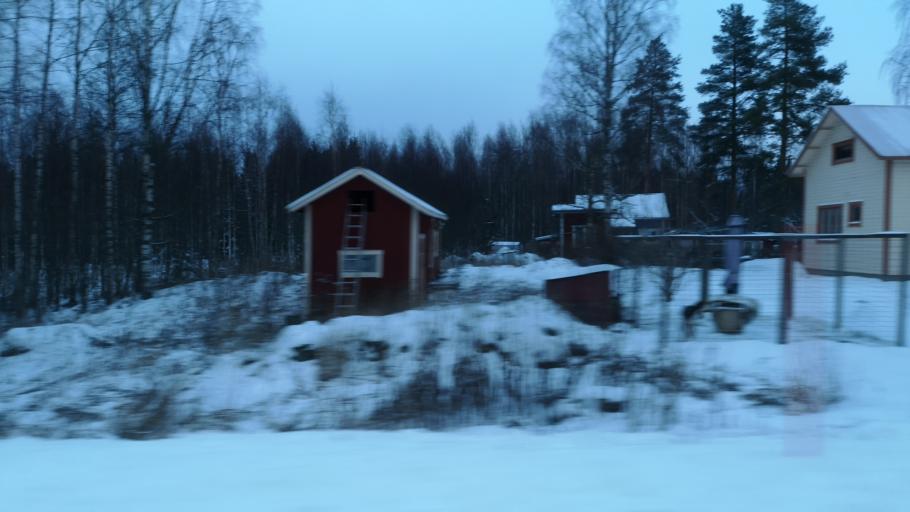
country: FI
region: Southern Savonia
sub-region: Savonlinna
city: Enonkoski
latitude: 62.1072
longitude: 28.6294
